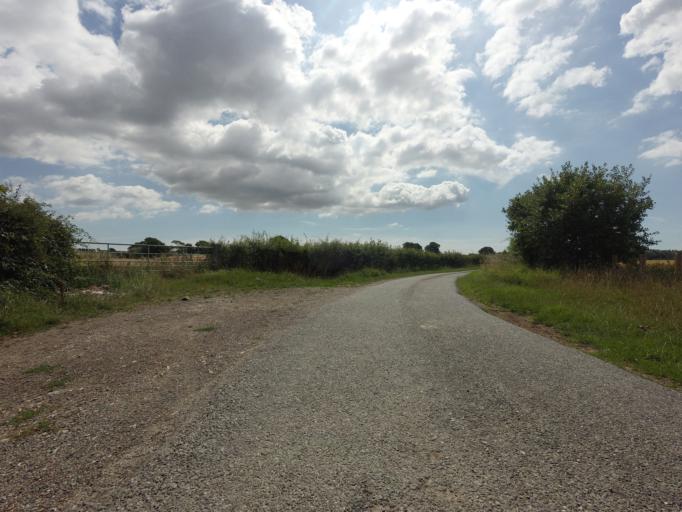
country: GB
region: England
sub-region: Kent
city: Stone
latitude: 51.0526
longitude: 0.7716
